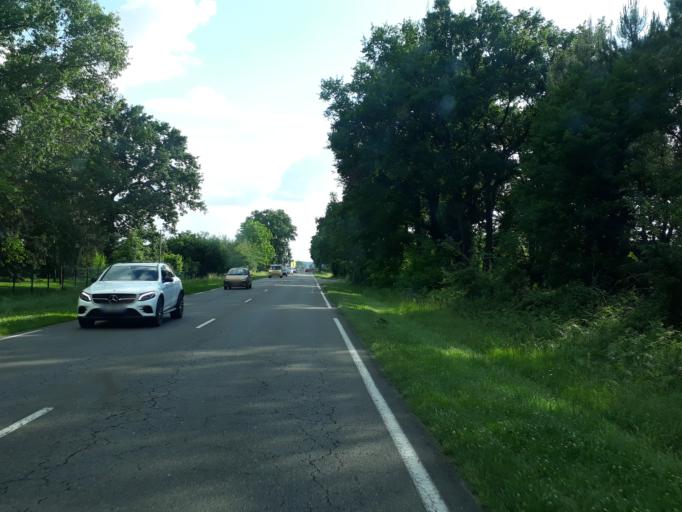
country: FR
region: Aquitaine
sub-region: Departement des Landes
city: Mont-de-Marsan
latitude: 43.9142
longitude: -0.4585
